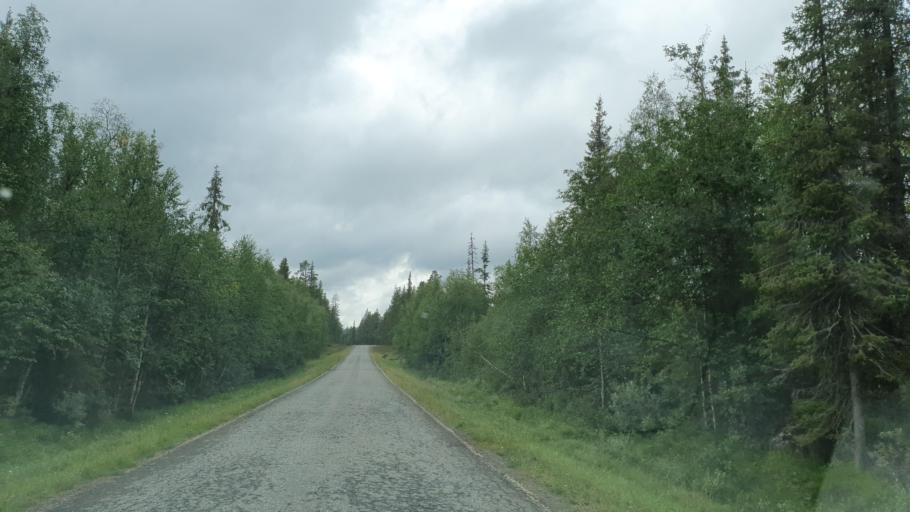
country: FI
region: Lapland
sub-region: Tunturi-Lappi
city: Muonio
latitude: 67.7346
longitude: 24.2711
